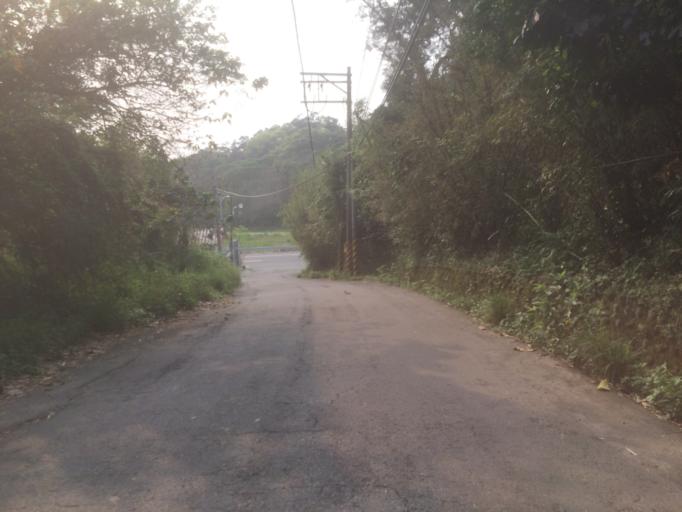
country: TW
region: Taiwan
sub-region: Hsinchu
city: Hsinchu
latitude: 24.7607
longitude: 120.9786
